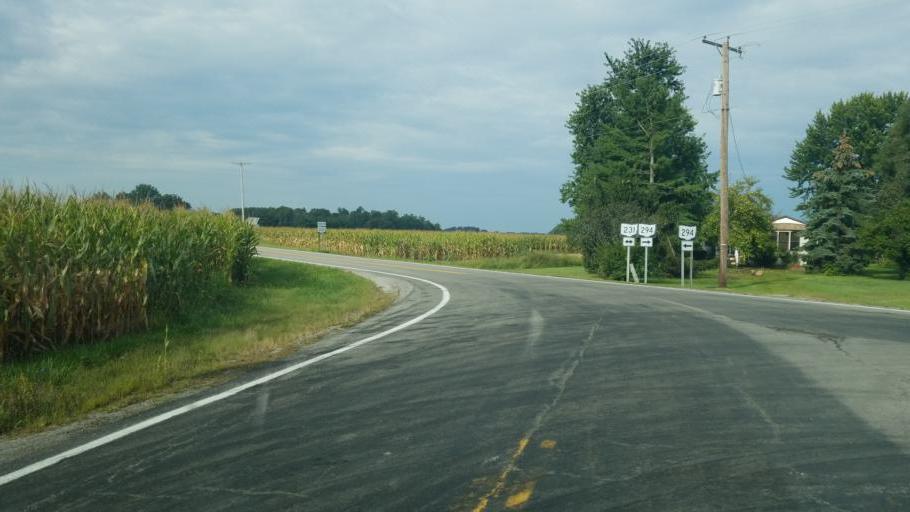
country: US
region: Ohio
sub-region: Marion County
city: Marion
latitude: 40.7173
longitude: -83.1256
